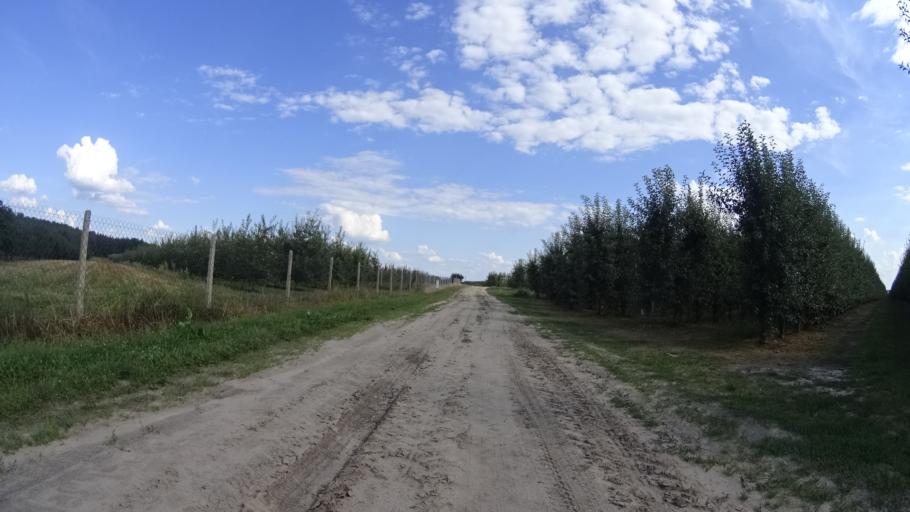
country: PL
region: Masovian Voivodeship
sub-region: Powiat bialobrzeski
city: Wysmierzyce
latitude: 51.6719
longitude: 20.7996
